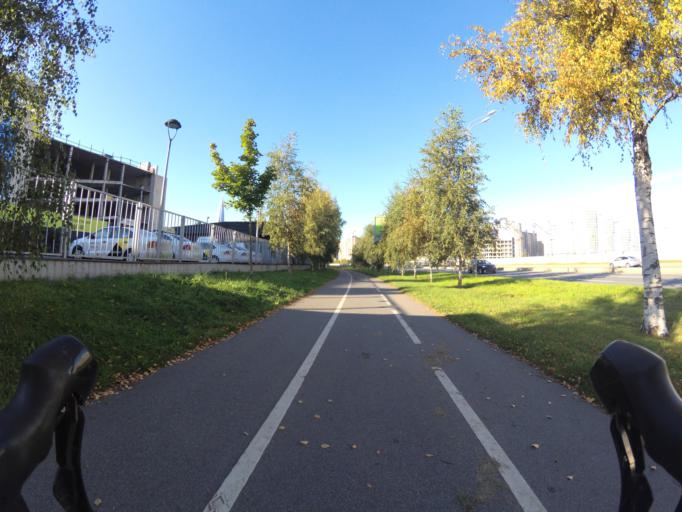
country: RU
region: Leningrad
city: Untolovo
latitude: 59.9941
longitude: 30.2110
